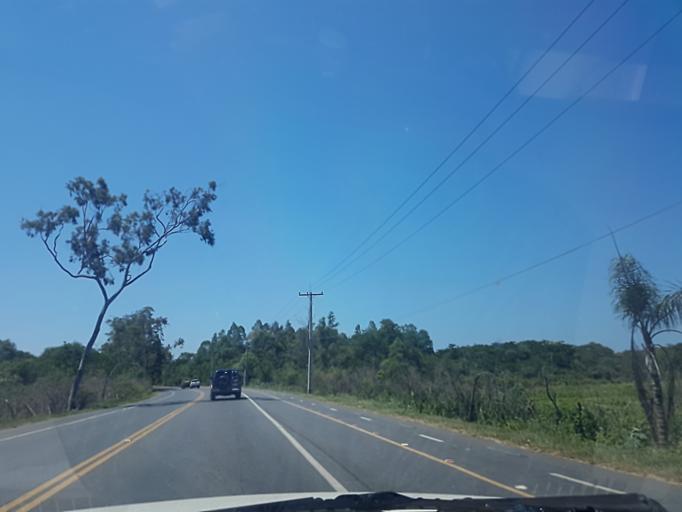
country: PY
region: Cordillera
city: San Bernardino
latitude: -25.2808
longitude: -57.3175
